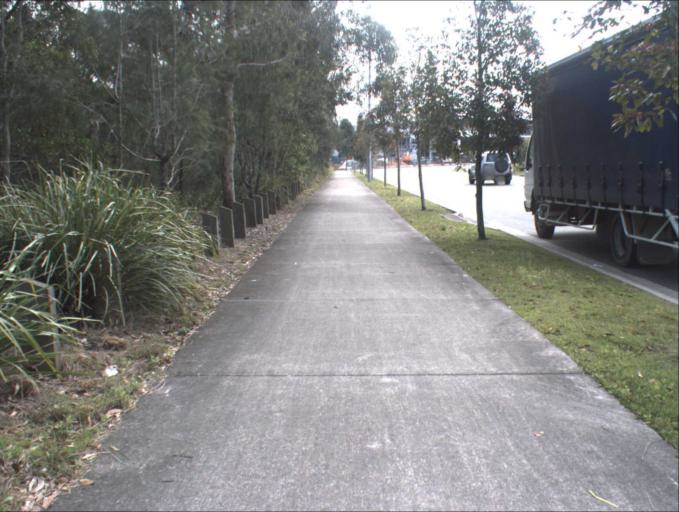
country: AU
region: Queensland
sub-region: Logan
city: Woodridge
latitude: -27.6706
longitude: 153.0752
